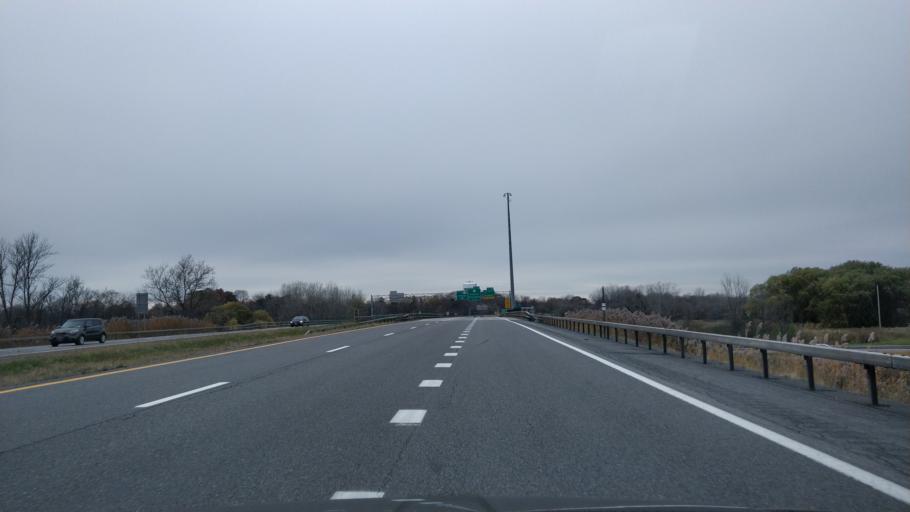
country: US
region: New York
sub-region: Onondaga County
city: North Syracuse
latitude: 43.1415
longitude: -76.1106
